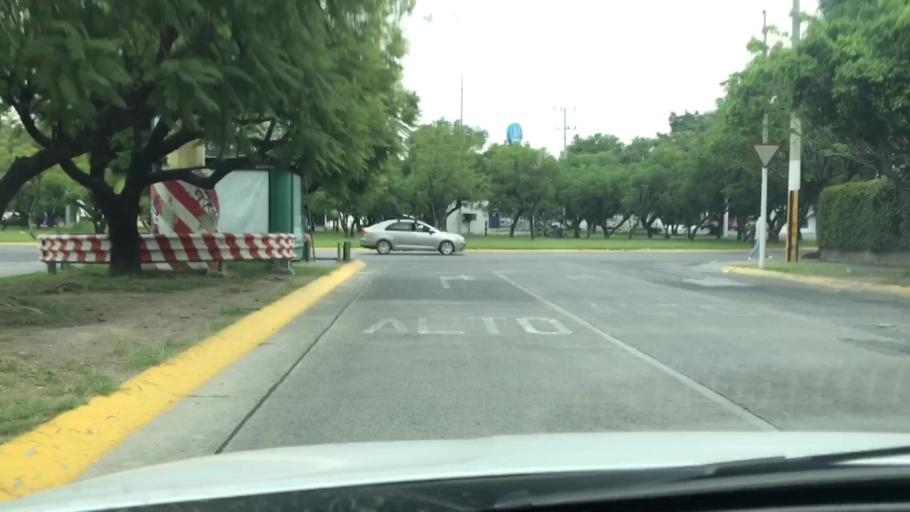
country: MX
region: Jalisco
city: Guadalajara
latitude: 20.6388
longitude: -103.4311
